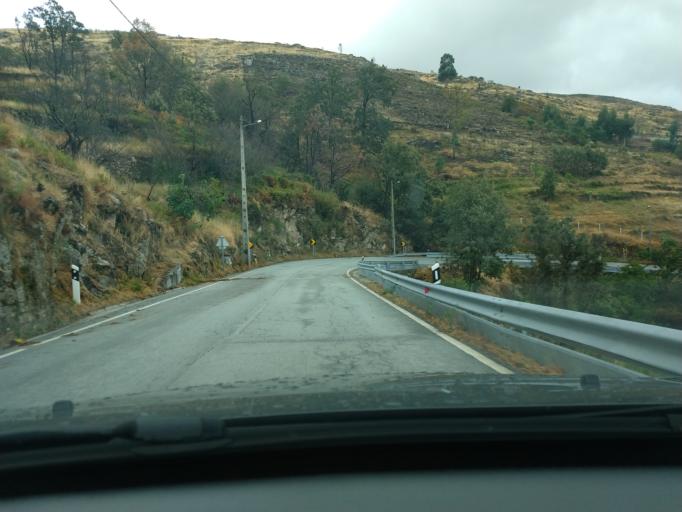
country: PT
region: Guarda
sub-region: Seia
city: Seia
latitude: 40.4153
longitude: -7.6883
